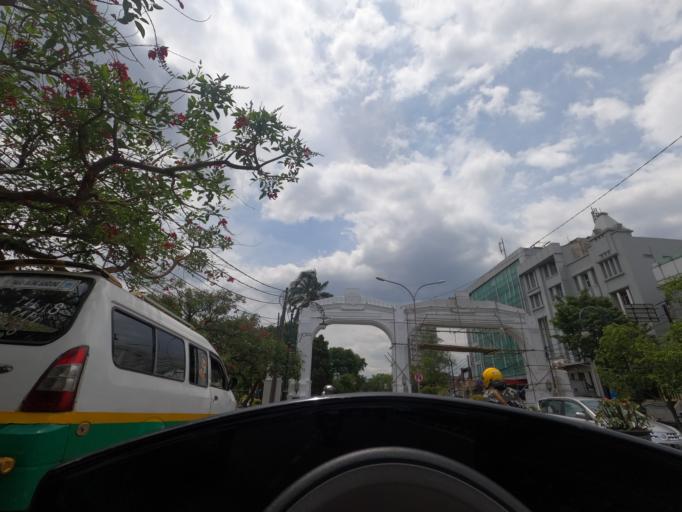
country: ID
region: West Java
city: Bandung
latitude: -6.9154
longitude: 107.6298
